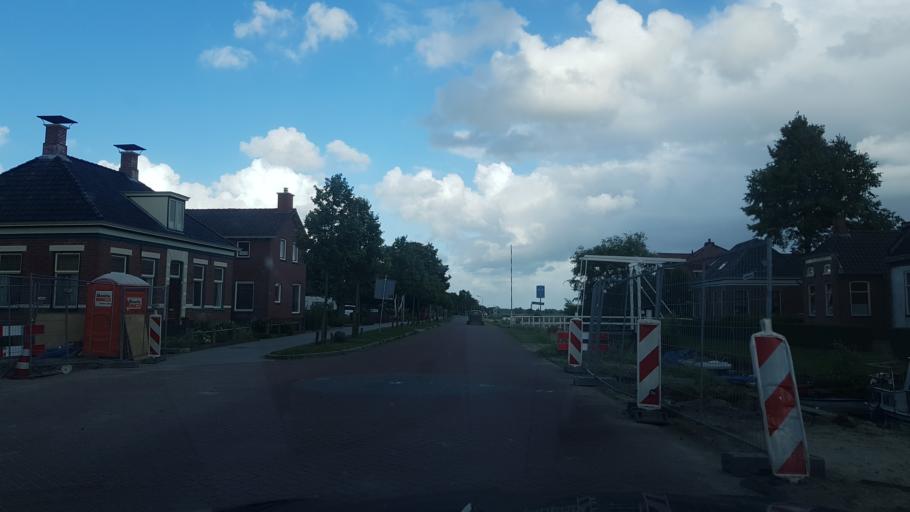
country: NL
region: Groningen
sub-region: Gemeente Appingedam
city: Appingedam
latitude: 53.3290
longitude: 6.7446
